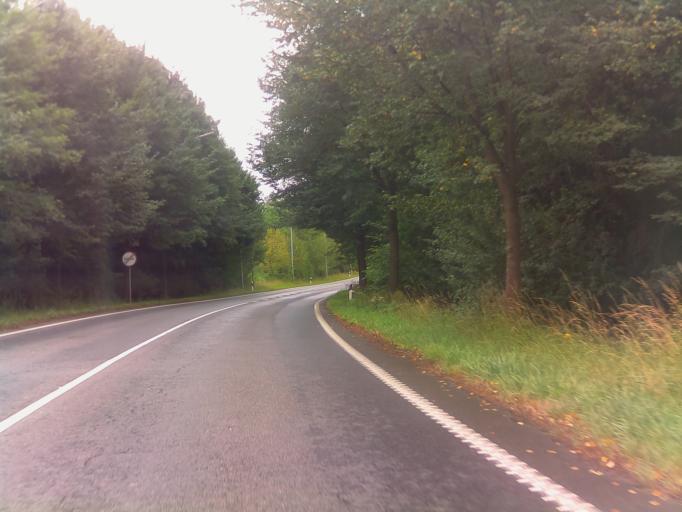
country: LU
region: Luxembourg
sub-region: Canton d'Esch-sur-Alzette
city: Reckange-sur-Mess
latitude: 49.5666
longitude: 6.0031
